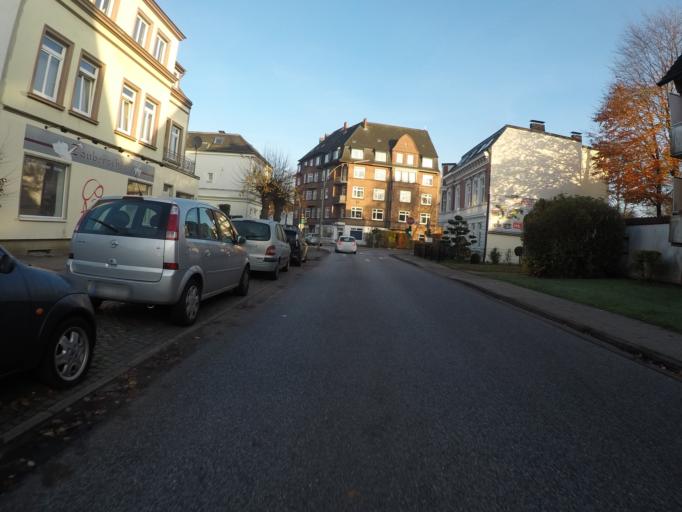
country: DE
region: Hamburg
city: Stellingen
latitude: 53.5964
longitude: 9.9328
